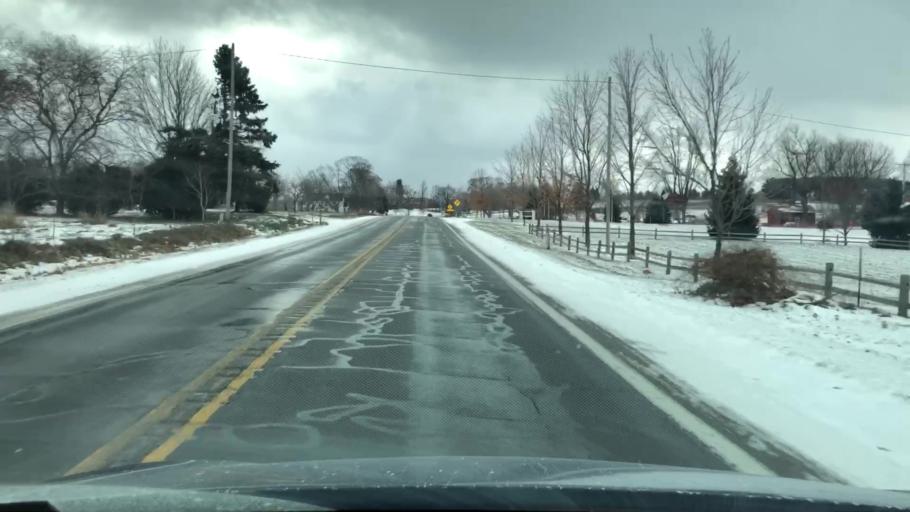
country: US
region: Michigan
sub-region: Antrim County
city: Elk Rapids
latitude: 44.8723
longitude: -85.5153
